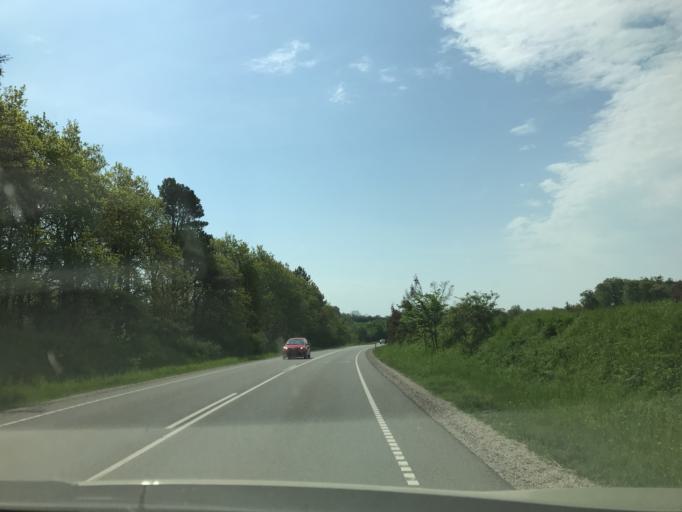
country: DK
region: South Denmark
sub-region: Middelfart Kommune
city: Ejby
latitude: 55.3869
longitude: 9.9168
